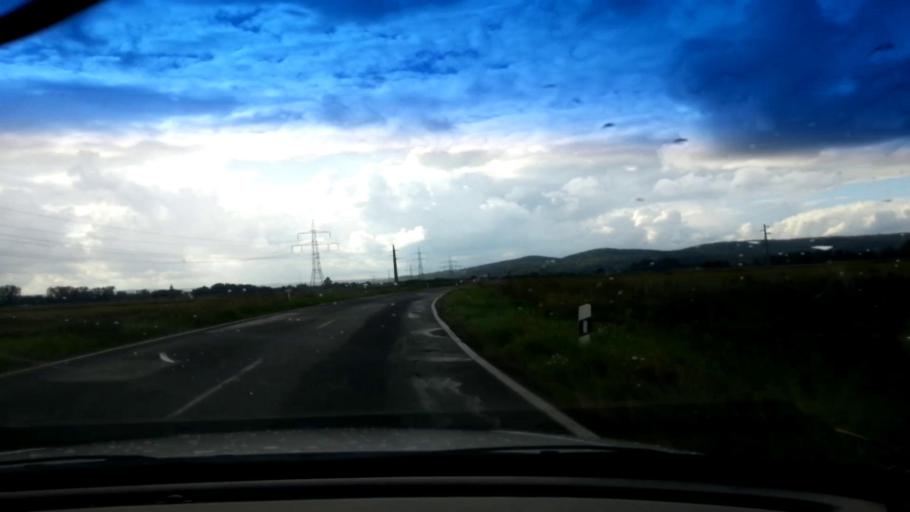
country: DE
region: Bavaria
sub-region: Upper Franconia
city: Gundelsheim
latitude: 49.9353
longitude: 10.9024
